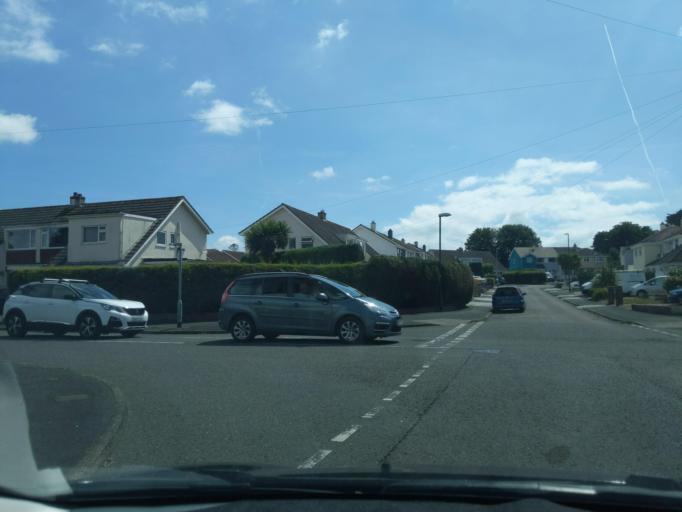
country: GB
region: England
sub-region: Borough of Torbay
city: Paignton
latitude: 50.4115
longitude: -3.5698
